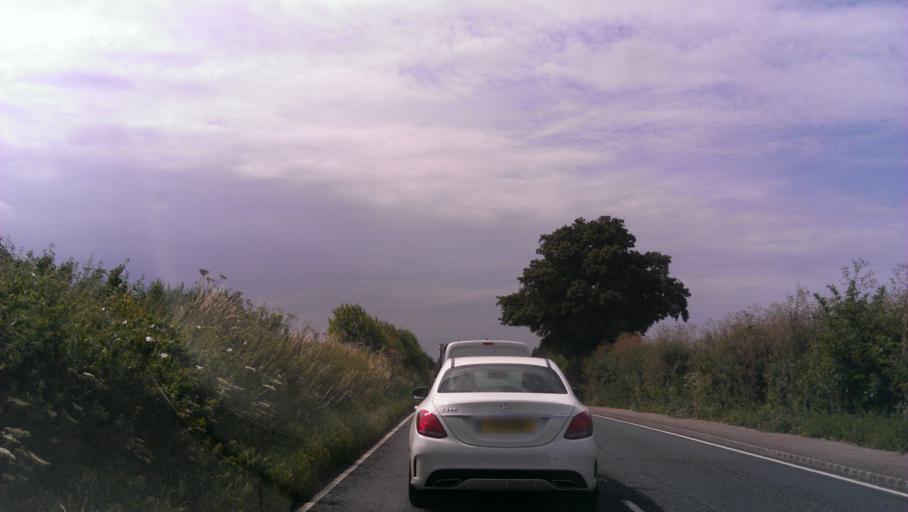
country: GB
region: England
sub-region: Kent
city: Teynham
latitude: 51.3223
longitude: 0.8219
